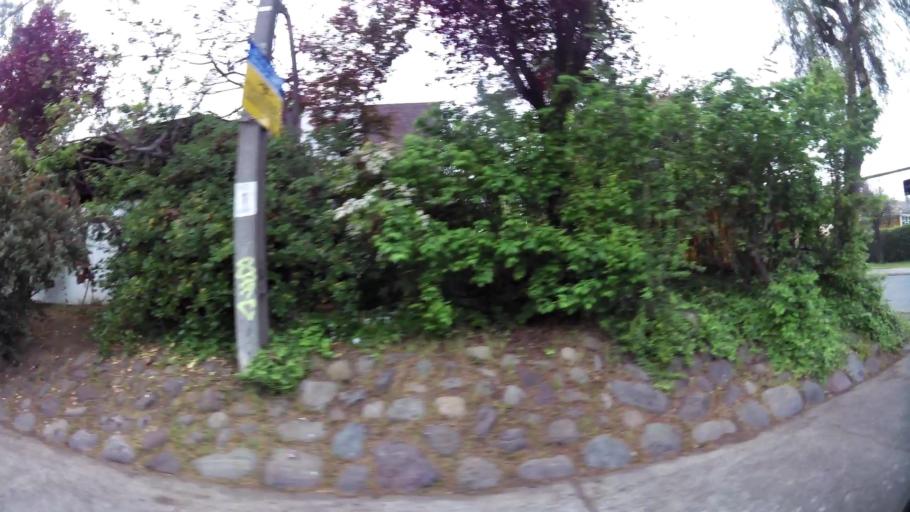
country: CL
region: Santiago Metropolitan
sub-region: Provincia de Santiago
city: Villa Presidente Frei, Nunoa, Santiago, Chile
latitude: -33.3892
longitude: -70.5573
